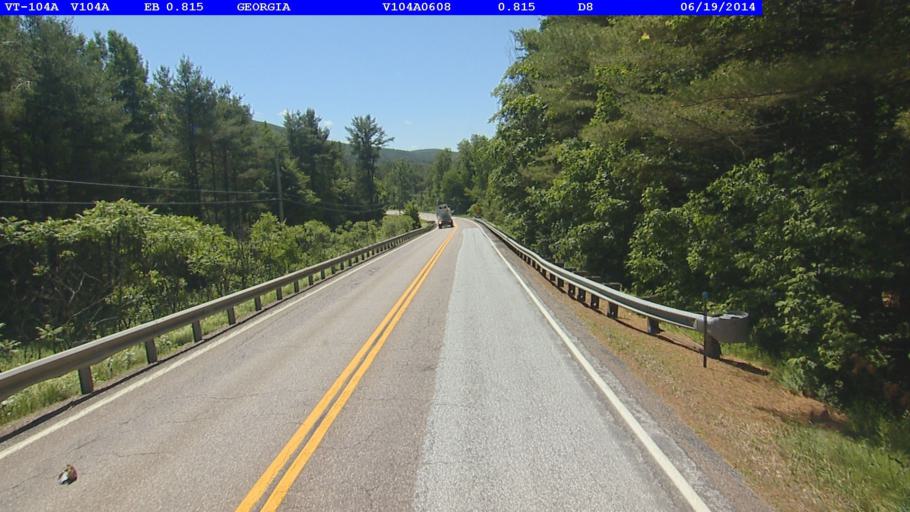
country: US
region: Vermont
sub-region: Chittenden County
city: Milton
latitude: 44.6864
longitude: -73.0967
